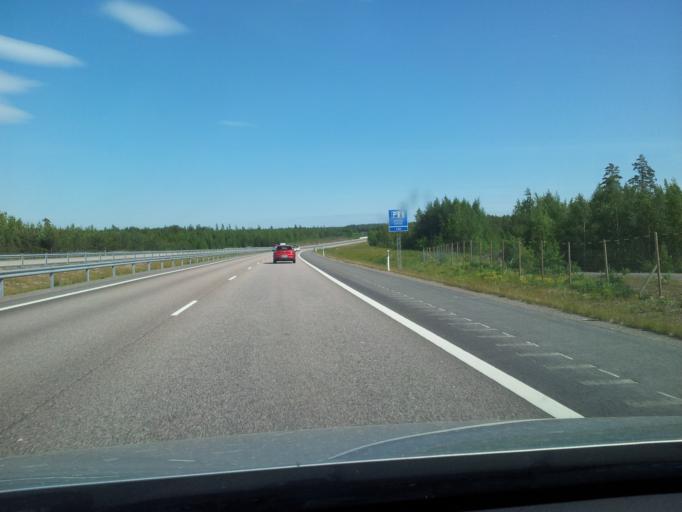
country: FI
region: Uusimaa
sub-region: Loviisa
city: Perna
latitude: 60.4771
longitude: 26.1030
